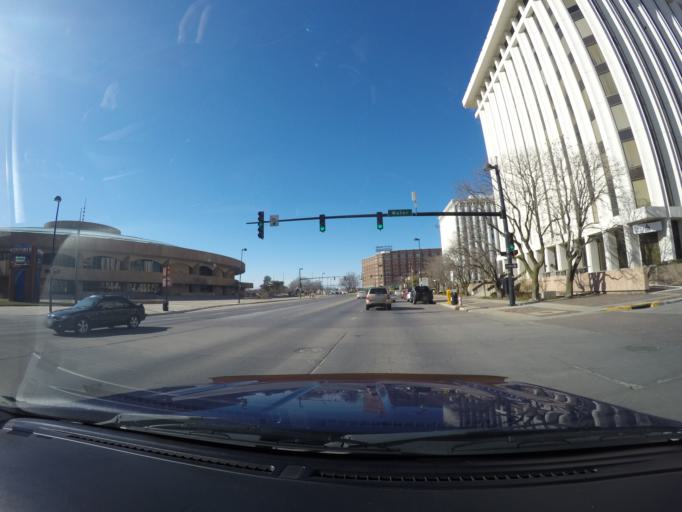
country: US
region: Kansas
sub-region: Sedgwick County
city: Wichita
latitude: 37.6860
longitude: -97.3395
